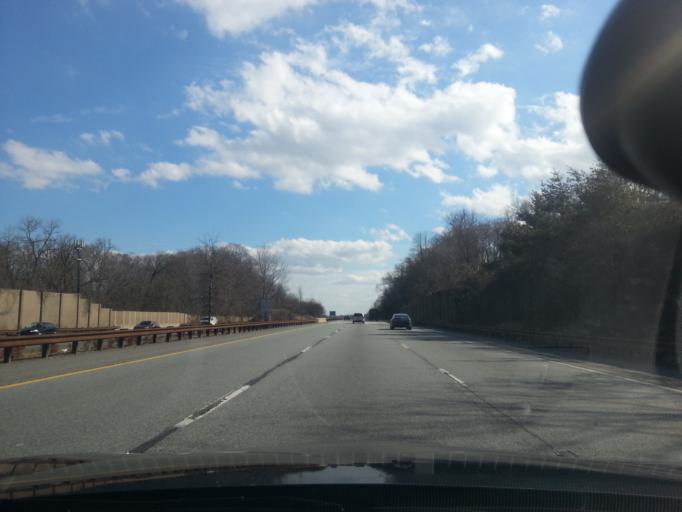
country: US
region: Pennsylvania
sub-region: Delaware County
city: Radnor
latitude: 40.0157
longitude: -75.3579
